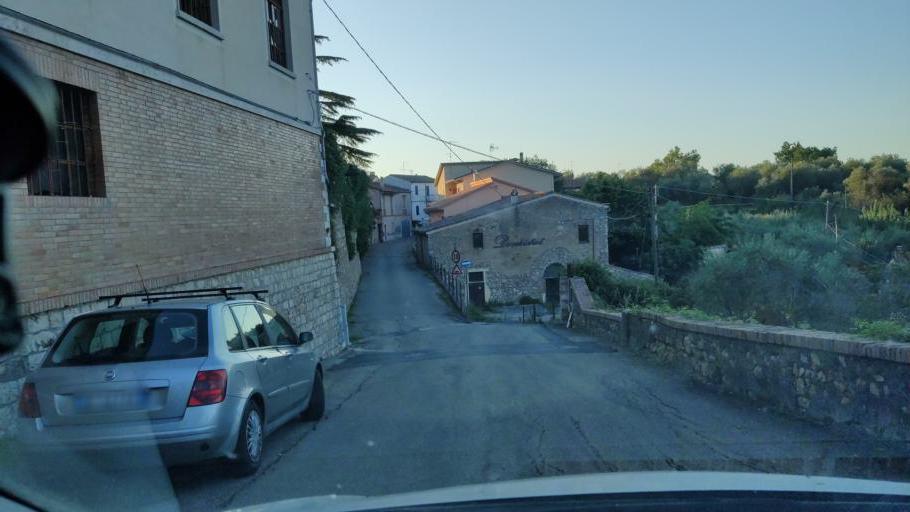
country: IT
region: Umbria
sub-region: Provincia di Terni
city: Giove
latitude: 42.5087
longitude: 12.3249
